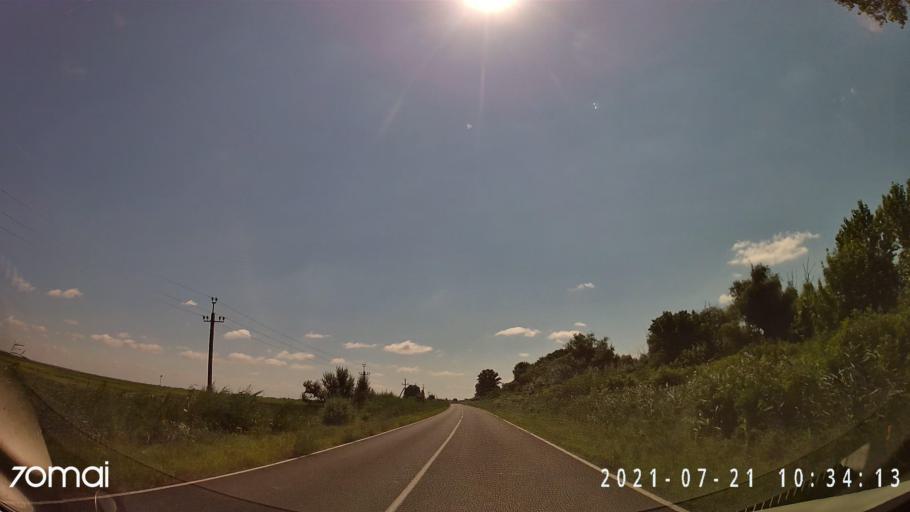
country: RO
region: Tulcea
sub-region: Oras Isaccea
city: Isaccea
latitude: 45.2963
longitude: 28.4428
